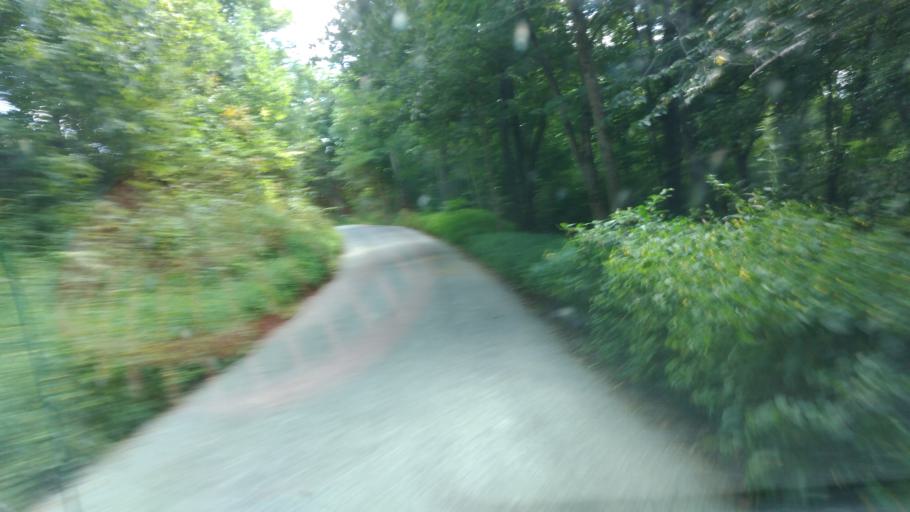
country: US
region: Ohio
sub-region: Holmes County
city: Millersburg
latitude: 40.6434
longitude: -81.8883
